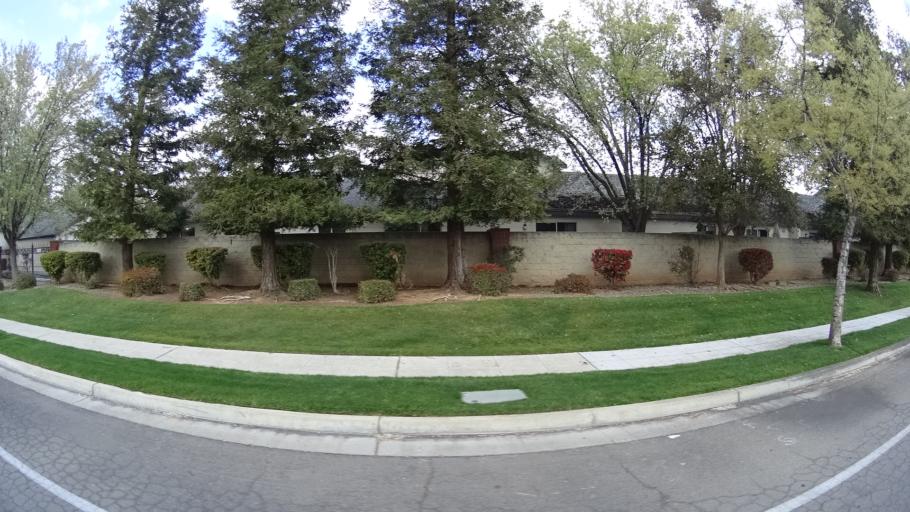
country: US
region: California
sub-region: Fresno County
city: Fresno
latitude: 36.8395
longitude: -119.8490
